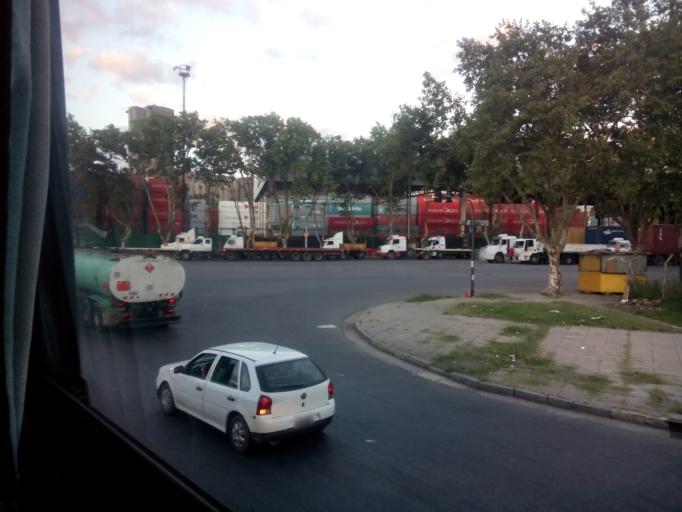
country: AR
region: Buenos Aires F.D.
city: Retiro
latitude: -34.5820
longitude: -58.3736
